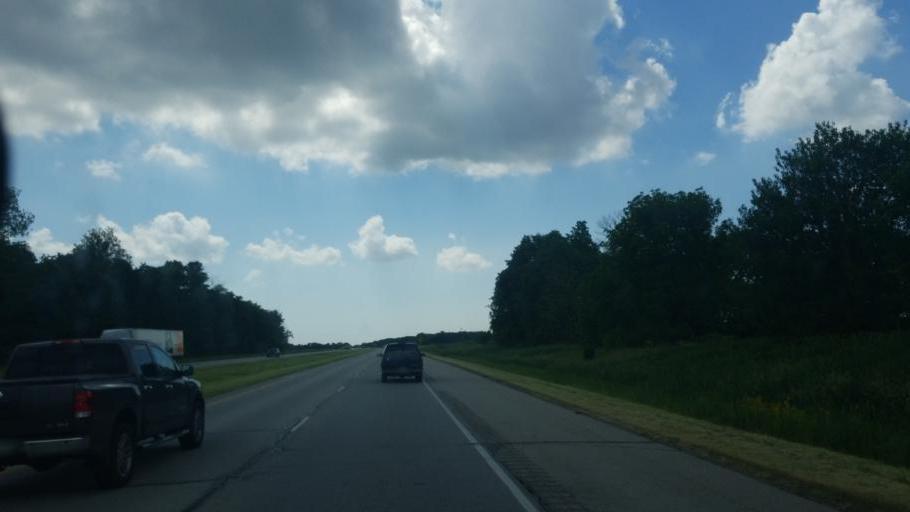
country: US
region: Indiana
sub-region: Kosciusko County
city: Warsaw
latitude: 41.2692
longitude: -85.9343
